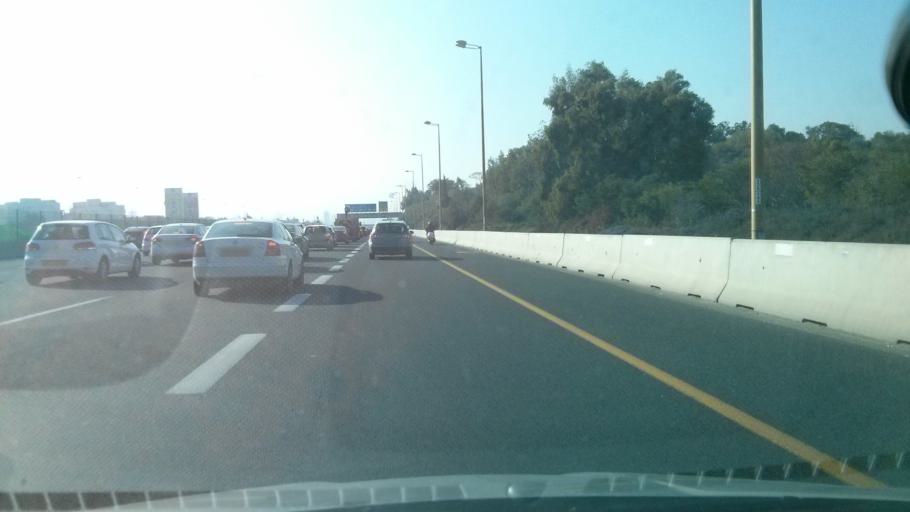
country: IL
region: Tel Aviv
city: Ramat HaSharon
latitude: 32.1293
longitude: 34.8098
